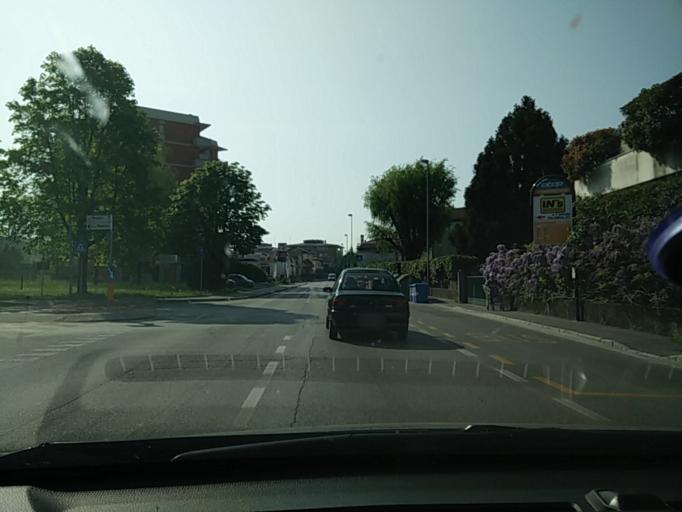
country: IT
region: Friuli Venezia Giulia
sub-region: Provincia di Pordenone
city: Pordenone
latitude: 45.9514
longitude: 12.6642
